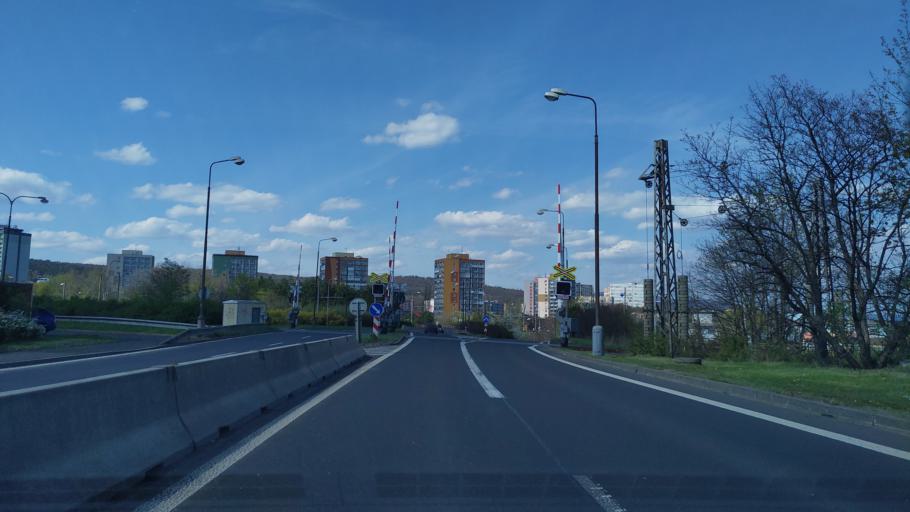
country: CZ
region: Ustecky
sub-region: Okres Chomutov
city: Chomutov
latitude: 50.4618
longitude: 13.4037
